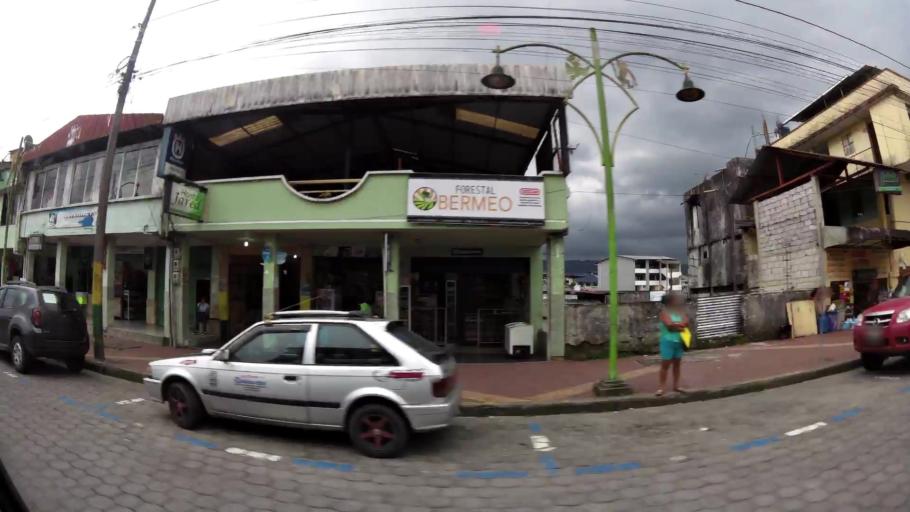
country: EC
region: Pastaza
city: Puyo
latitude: -1.4881
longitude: -77.9993
